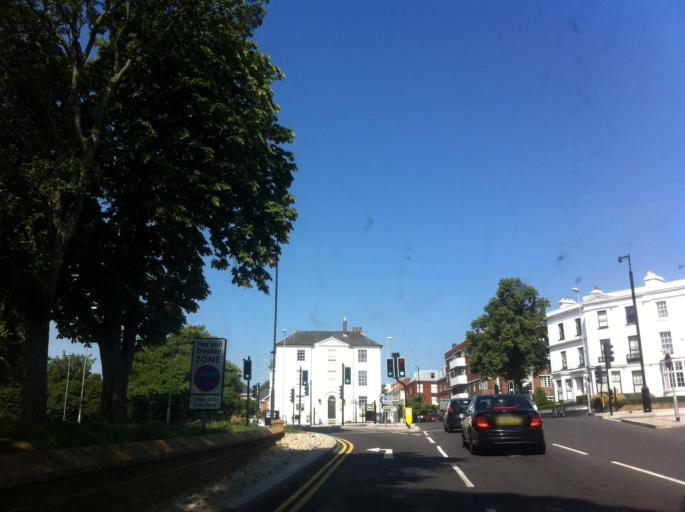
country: GB
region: England
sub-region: Northamptonshire
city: Northampton
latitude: 52.2342
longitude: -0.8867
